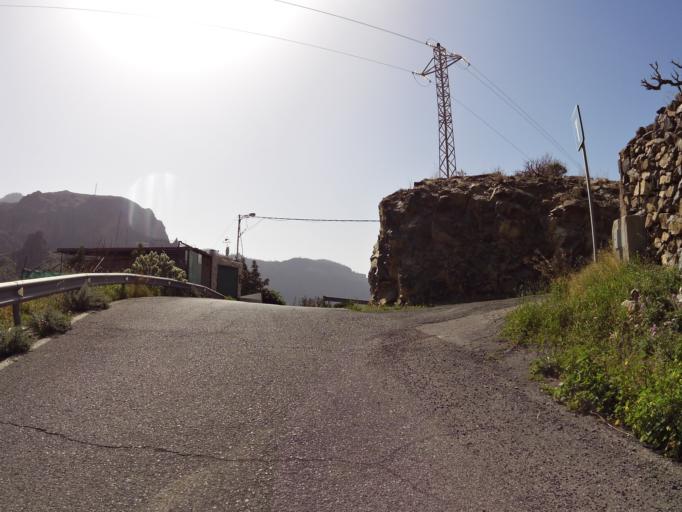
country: ES
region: Canary Islands
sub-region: Provincia de Las Palmas
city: Mogan
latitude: 27.9057
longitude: -15.6713
